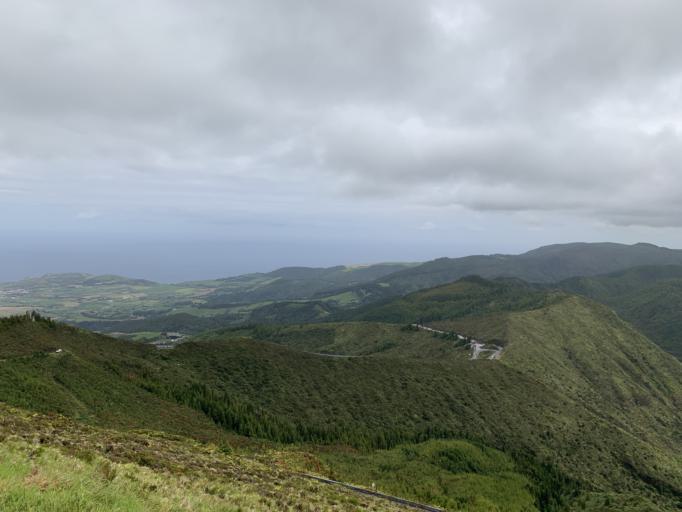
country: PT
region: Azores
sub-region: Vila Franca do Campo
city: Vila Franca do Campo
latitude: 37.7646
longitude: -25.4954
